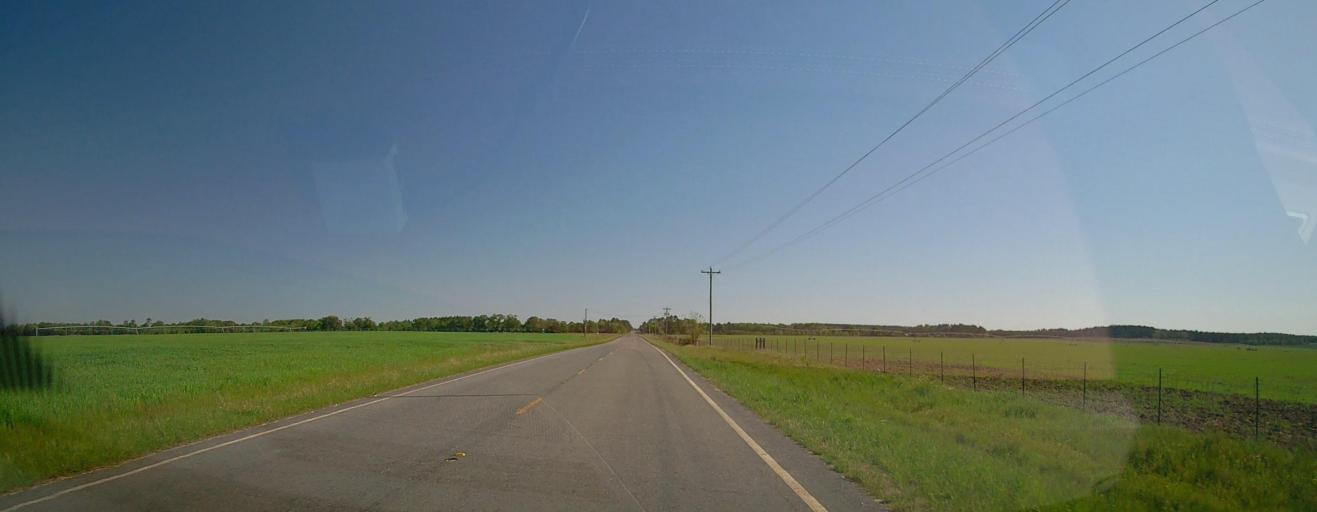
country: US
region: Georgia
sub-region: Wilcox County
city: Rochelle
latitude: 32.0765
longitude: -83.5035
